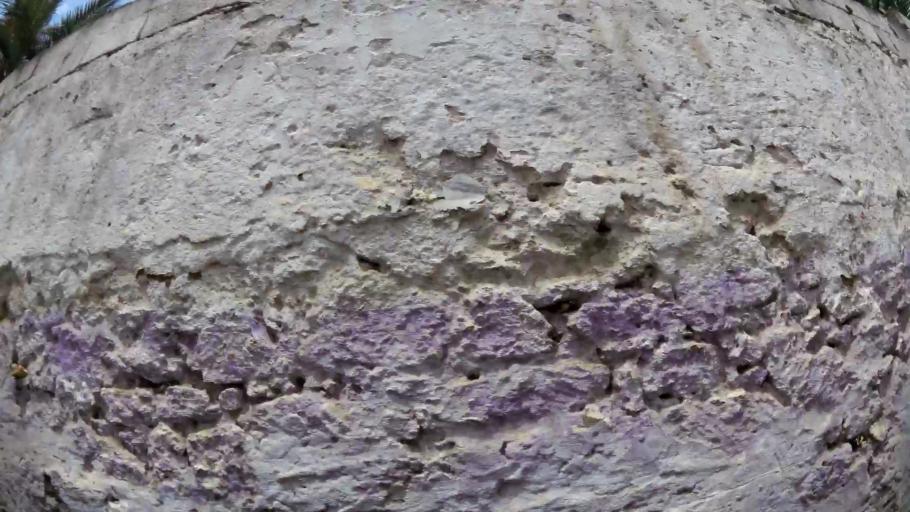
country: MA
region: Rabat-Sale-Zemmour-Zaer
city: Sale
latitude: 34.0357
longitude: -6.8085
